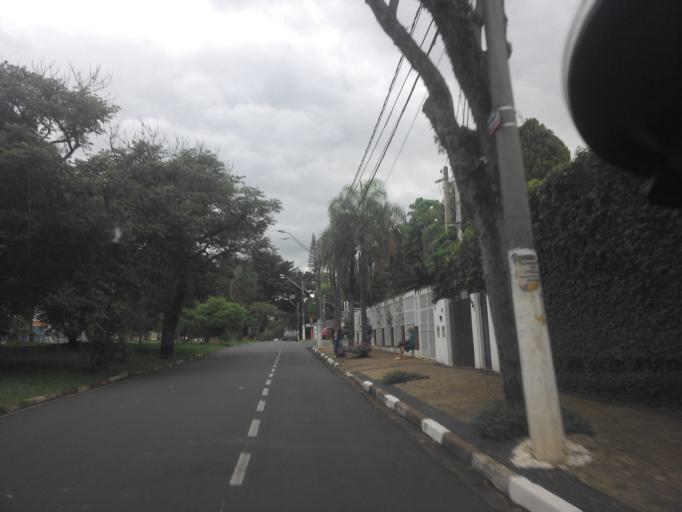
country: BR
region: Sao Paulo
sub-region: Campinas
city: Campinas
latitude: -22.8202
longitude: -47.0750
